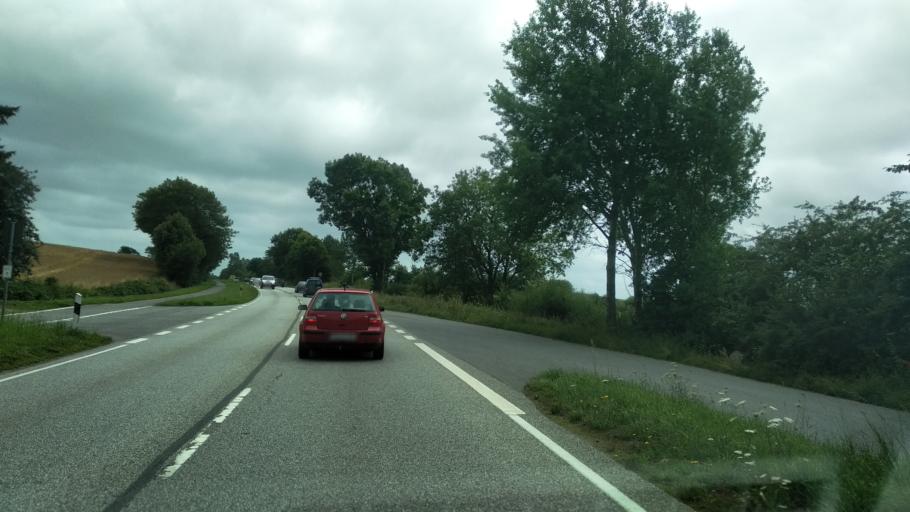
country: DE
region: Schleswig-Holstein
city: Oeversee
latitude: 54.7129
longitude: 9.4404
